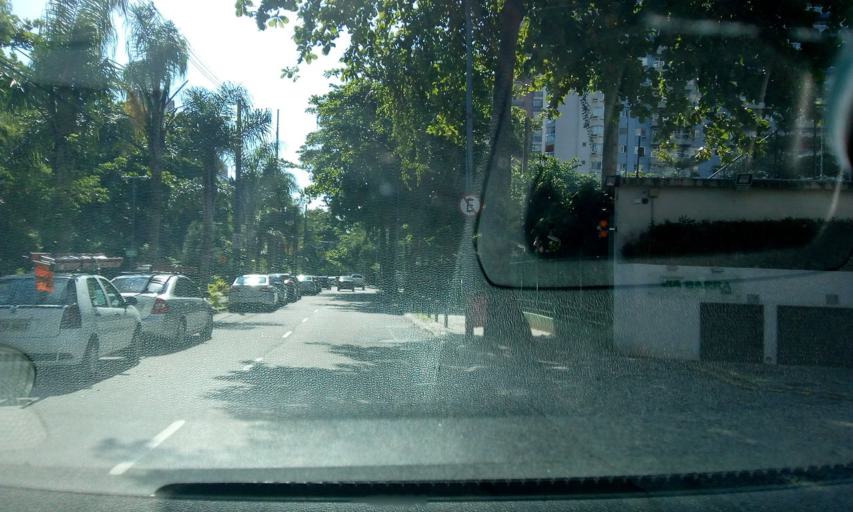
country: BR
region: Rio de Janeiro
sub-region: Rio De Janeiro
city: Rio de Janeiro
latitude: -23.0076
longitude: -43.3233
